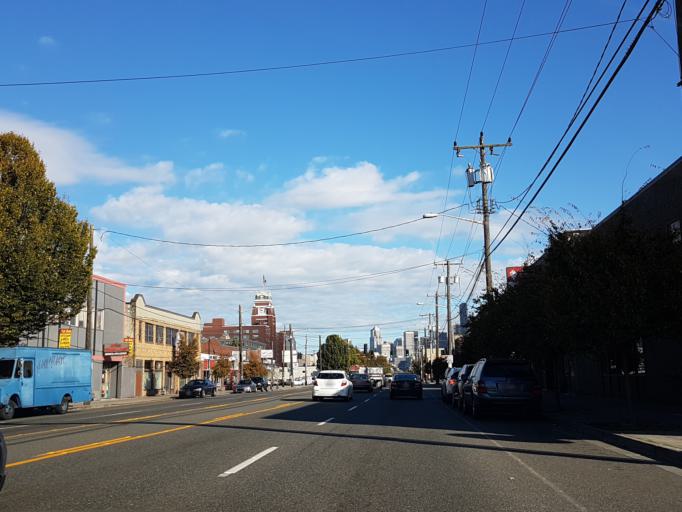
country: US
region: Washington
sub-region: King County
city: Seattle
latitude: 47.5766
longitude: -122.3341
